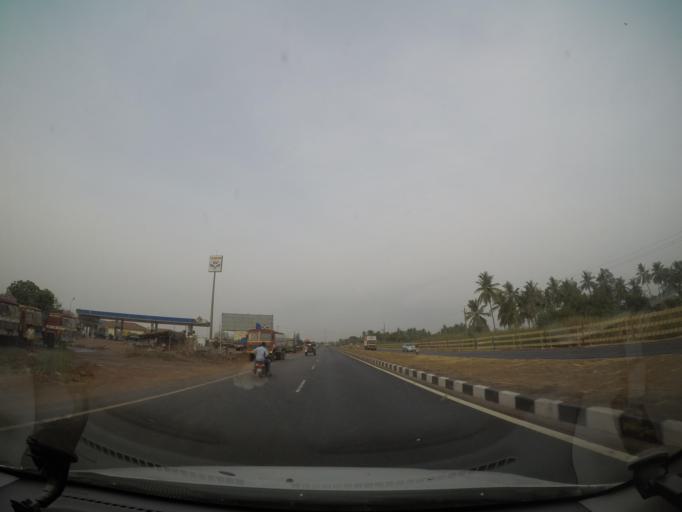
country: IN
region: Andhra Pradesh
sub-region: Krishna
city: Gannavaram
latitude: 16.6047
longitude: 80.9020
